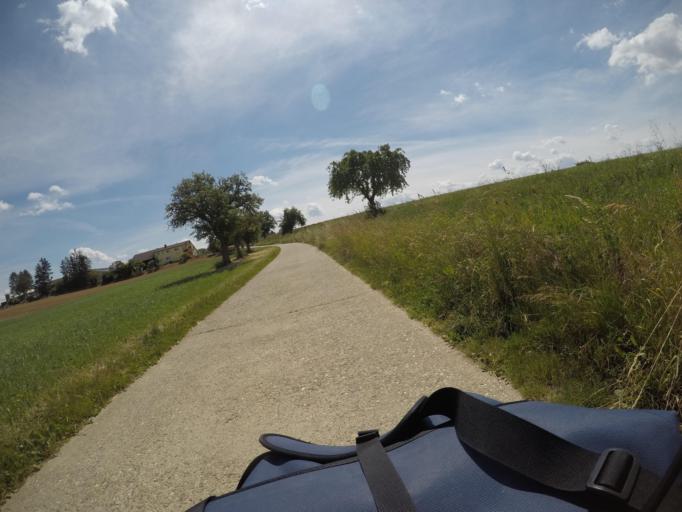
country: DE
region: Baden-Wuerttemberg
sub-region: Karlsruhe Region
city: Sinsheim
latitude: 49.2084
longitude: 8.8814
